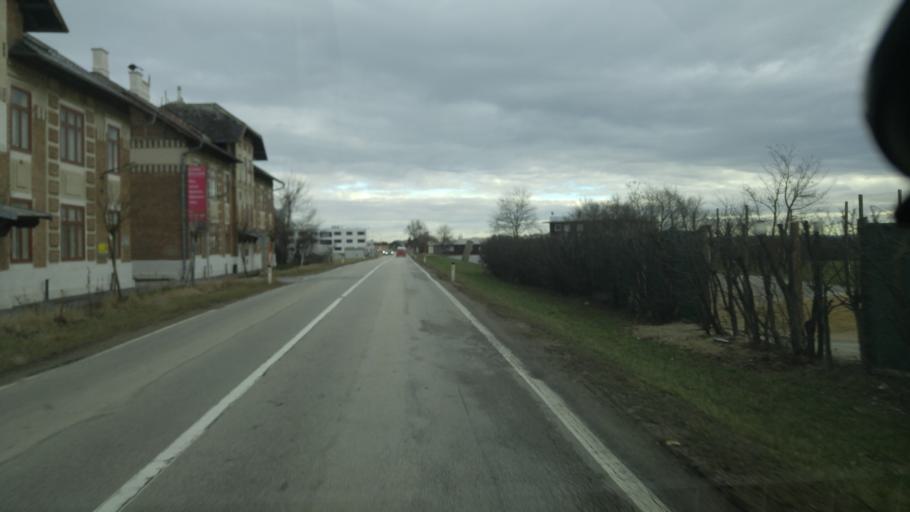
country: AT
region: Lower Austria
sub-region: Politischer Bezirk Modling
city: Laxenburg
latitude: 48.0816
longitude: 16.3661
